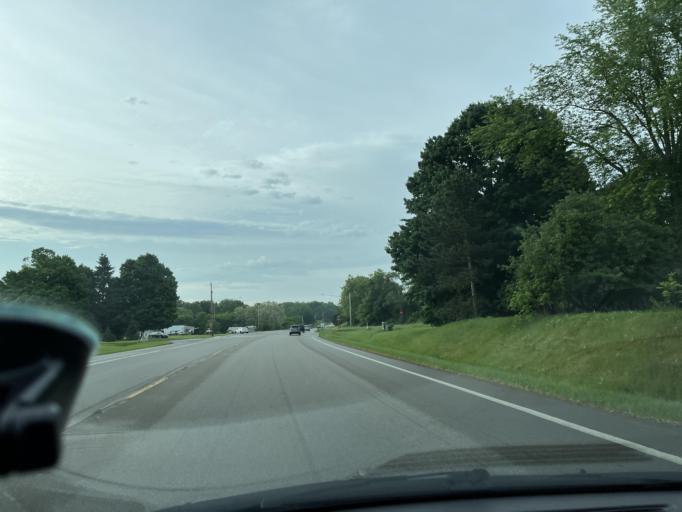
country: US
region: Michigan
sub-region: Barry County
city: Hastings
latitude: 42.6537
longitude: -85.3445
